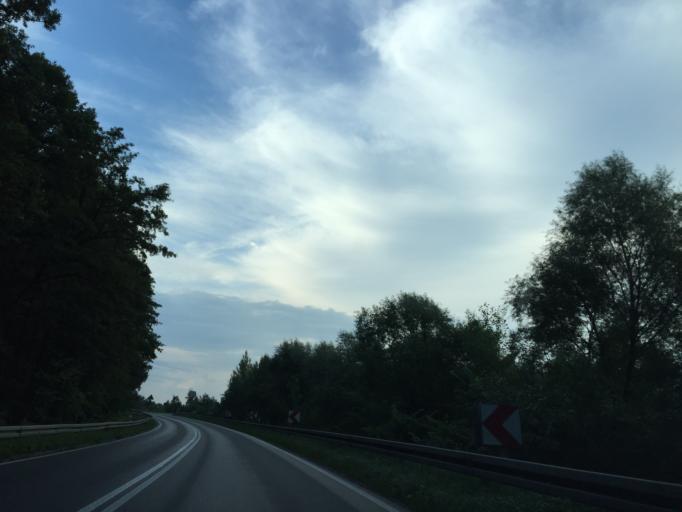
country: PL
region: Masovian Voivodeship
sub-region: Powiat ostrowski
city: Brok
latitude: 52.6898
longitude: 21.8523
